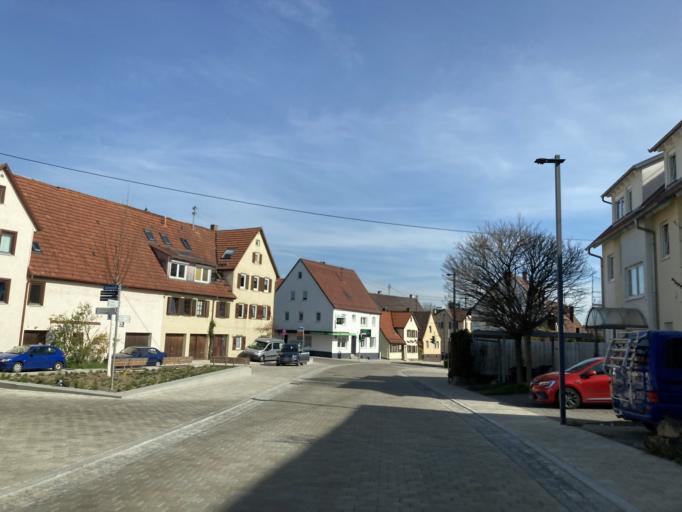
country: DE
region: Baden-Wuerttemberg
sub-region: Tuebingen Region
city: Nehren
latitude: 48.4287
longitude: 9.0675
